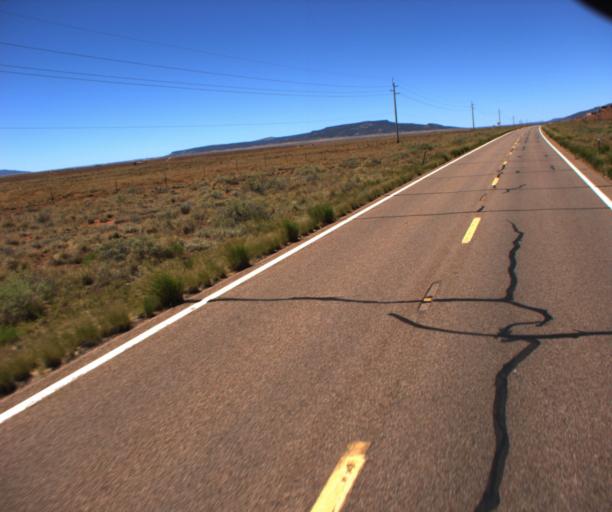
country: US
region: Arizona
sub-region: Coconino County
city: LeChee
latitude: 34.9317
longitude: -110.7959
